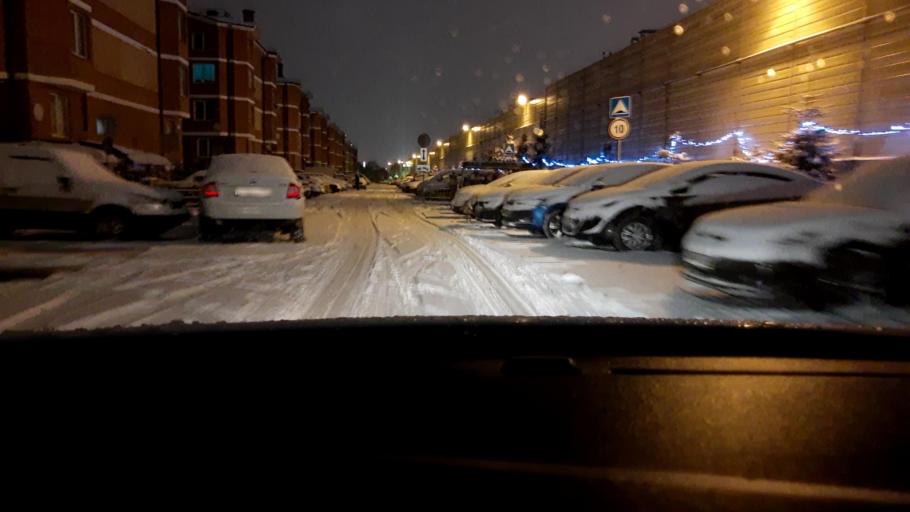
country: RU
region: Moskovskaya
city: Novoivanovskoye
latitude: 55.7098
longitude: 37.3571
